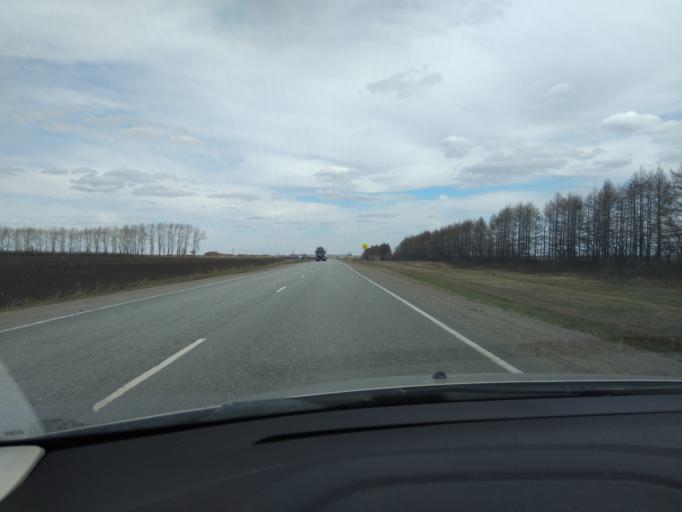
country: RU
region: Sverdlovsk
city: Yelanskiy
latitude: 56.7737
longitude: 62.4540
